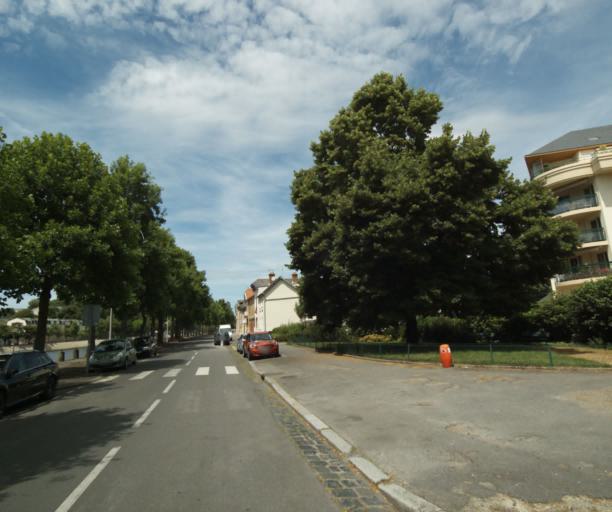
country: FR
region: Pays de la Loire
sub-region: Departement de la Mayenne
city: Laval
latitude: 48.0613
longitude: -0.7623
